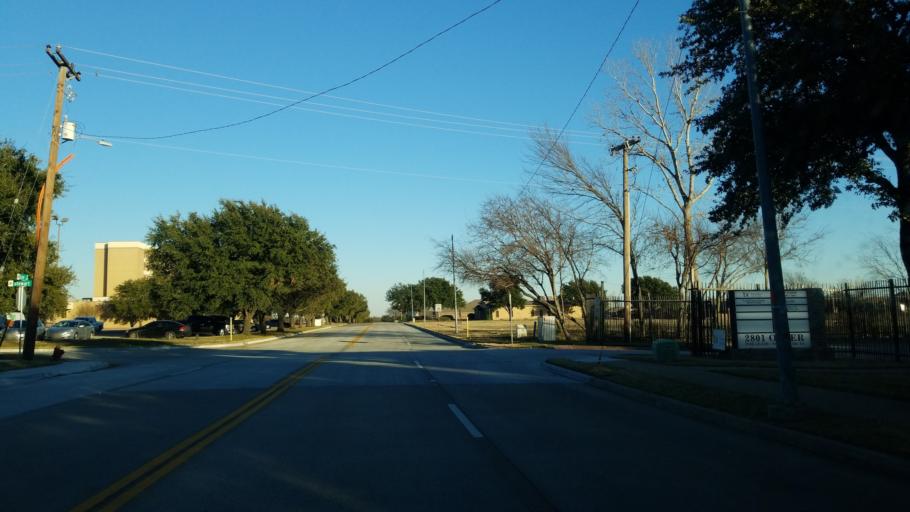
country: US
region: Texas
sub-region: Dallas County
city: Grand Prairie
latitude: 32.7319
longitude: -97.0517
